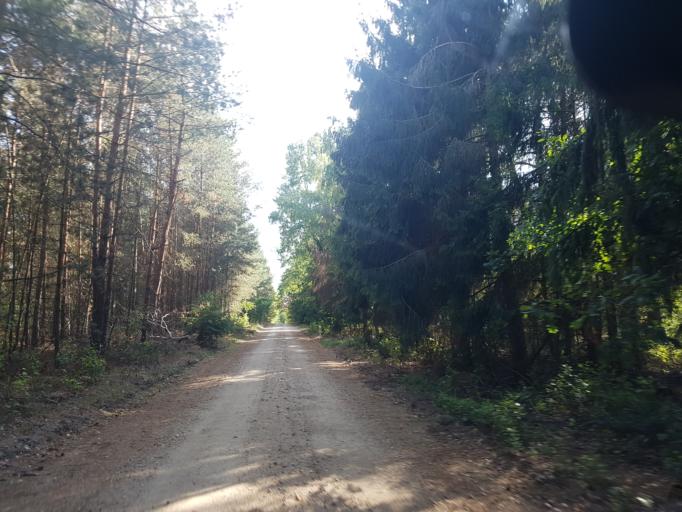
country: DE
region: Brandenburg
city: Gorzke
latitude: 52.0440
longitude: 12.2942
